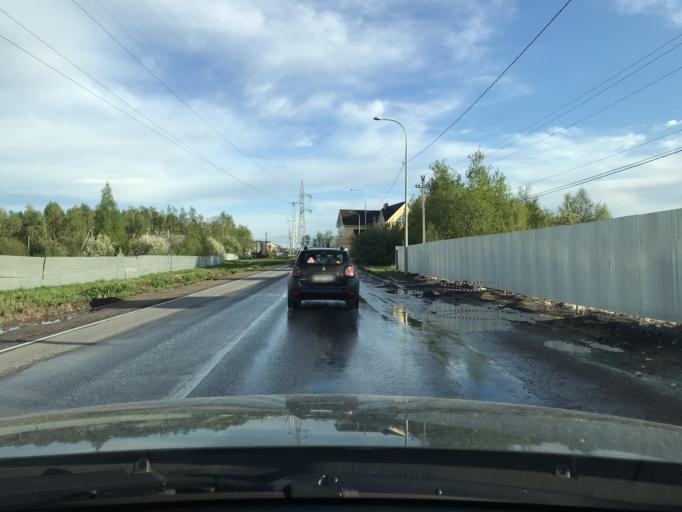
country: RU
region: Moskovskaya
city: Naro-Fominsk
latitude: 55.3809
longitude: 36.6997
